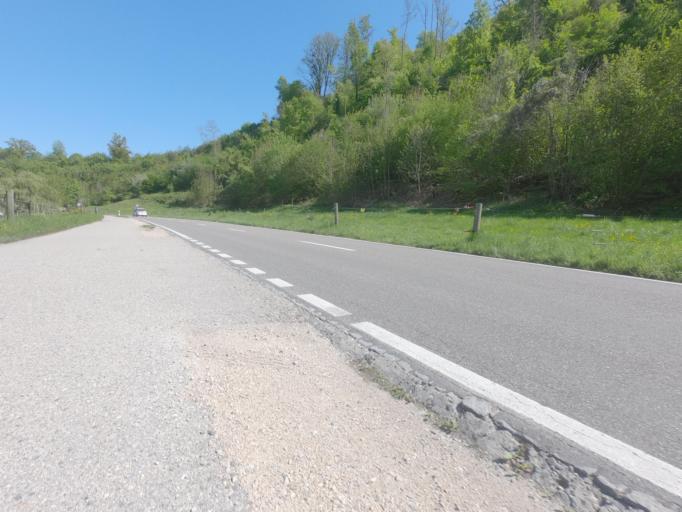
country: CH
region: Bern
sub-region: Seeland District
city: Erlach
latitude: 47.0441
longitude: 7.0896
